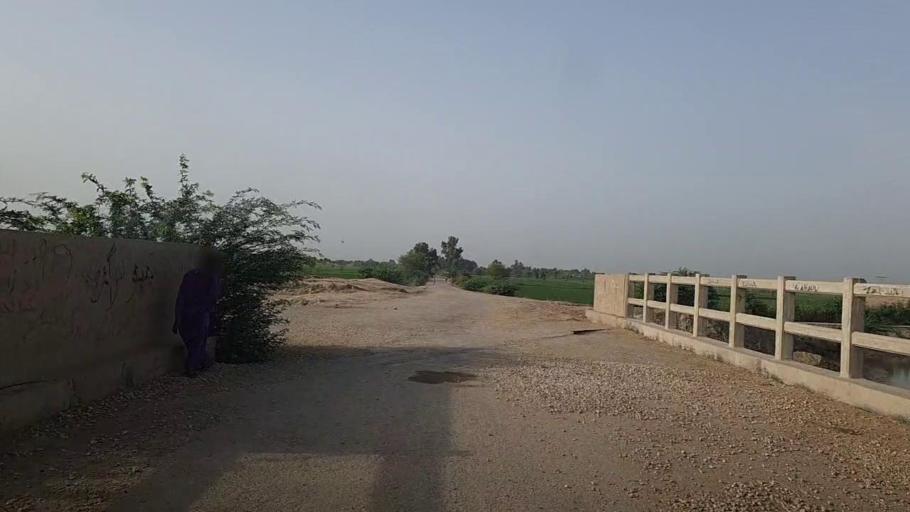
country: PK
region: Sindh
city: Mehar
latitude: 27.1277
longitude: 67.7891
